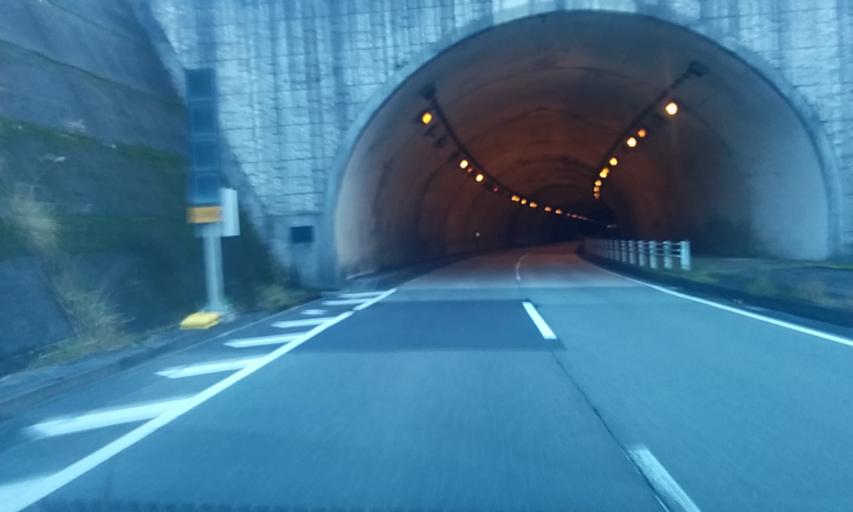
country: JP
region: Hyogo
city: Sasayama
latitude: 35.0731
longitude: 135.3811
